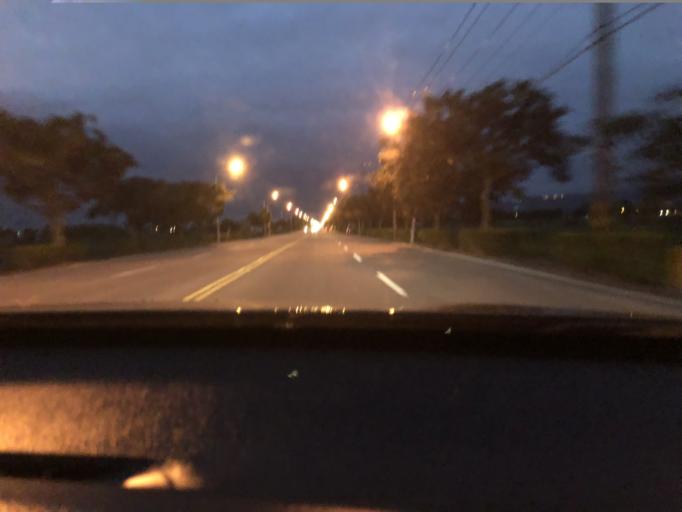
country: TW
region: Taiwan
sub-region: Hualien
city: Hualian
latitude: 23.9498
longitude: 121.5638
